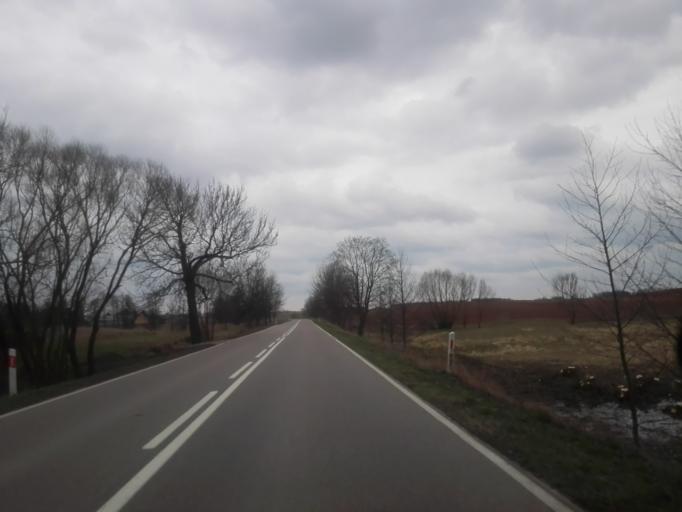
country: PL
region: Podlasie
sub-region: Powiat sejnenski
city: Sejny
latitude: 54.0887
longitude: 23.3457
